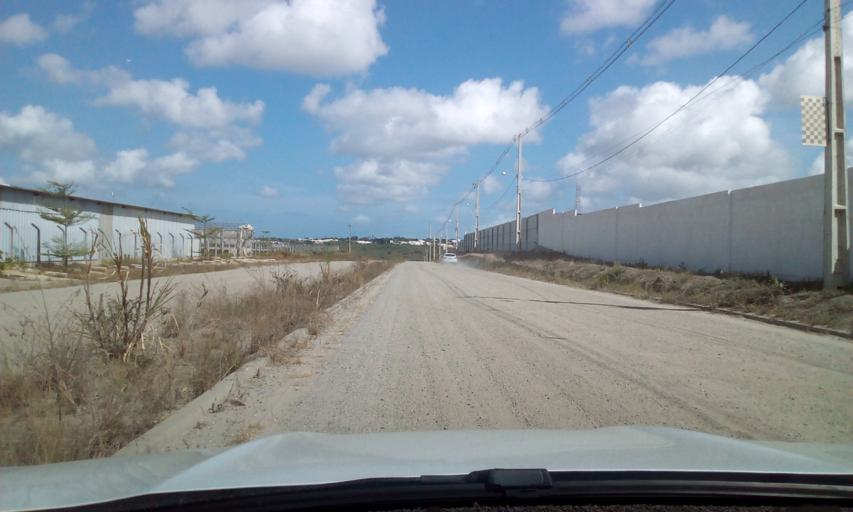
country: BR
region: Paraiba
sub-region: Conde
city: Conde
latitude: -7.2512
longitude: -34.9299
